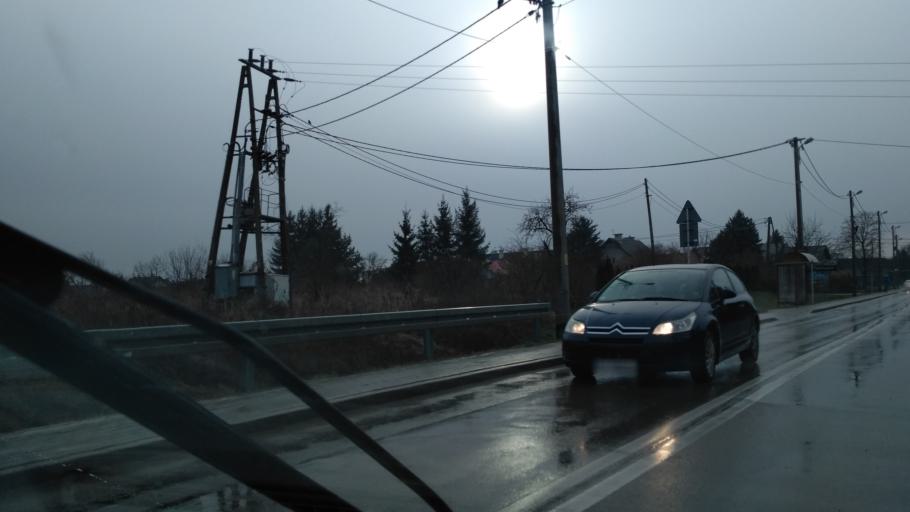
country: PL
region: Subcarpathian Voivodeship
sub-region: Rzeszow
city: Rzeszow
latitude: 49.9995
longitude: 21.9912
